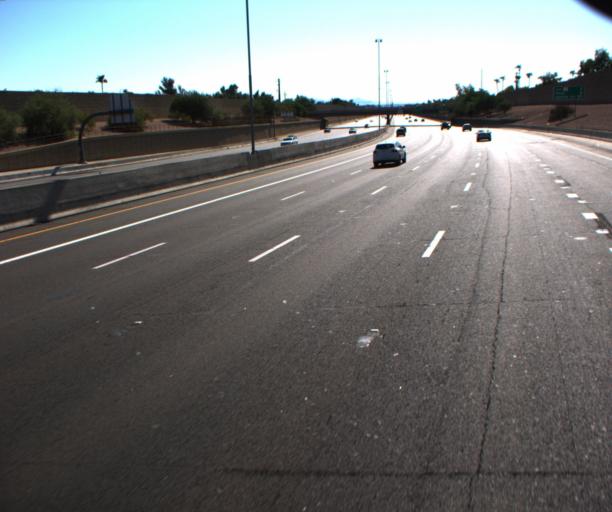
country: US
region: Arizona
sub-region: Maricopa County
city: Guadalupe
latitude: 33.3855
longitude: -111.9553
